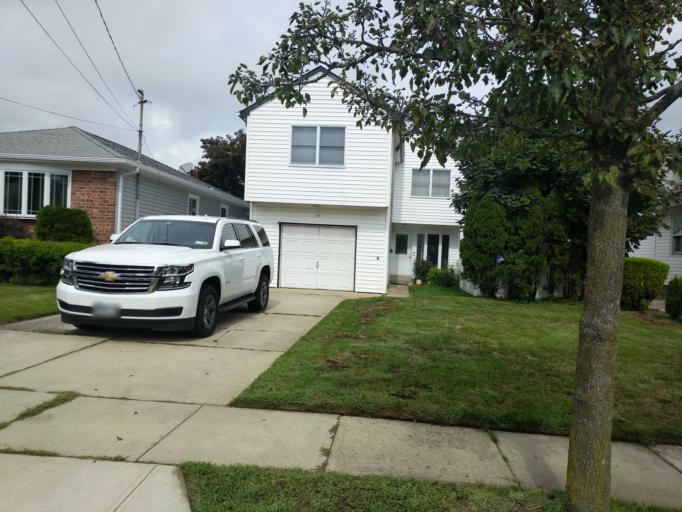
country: US
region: New York
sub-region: Nassau County
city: Valley Stream
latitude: 40.6668
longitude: -73.6919
